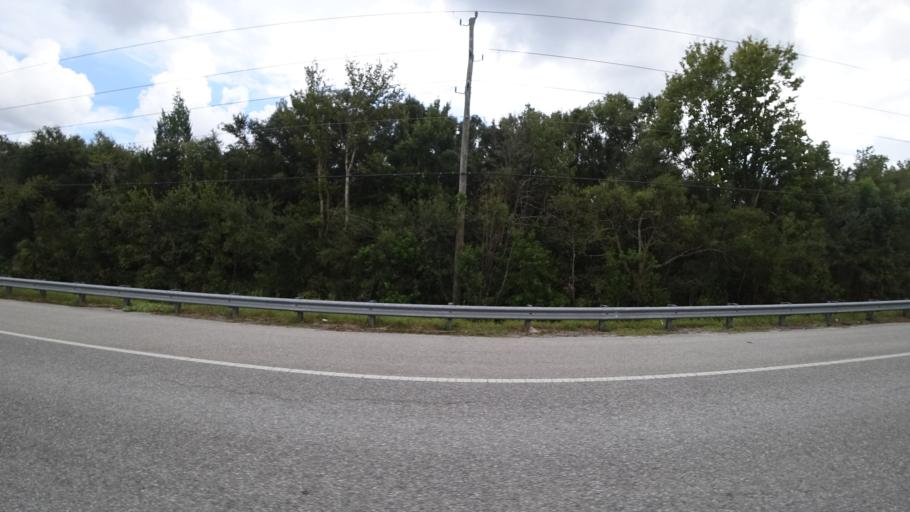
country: US
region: Florida
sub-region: Manatee County
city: Ellenton
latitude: 27.5094
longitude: -82.3686
